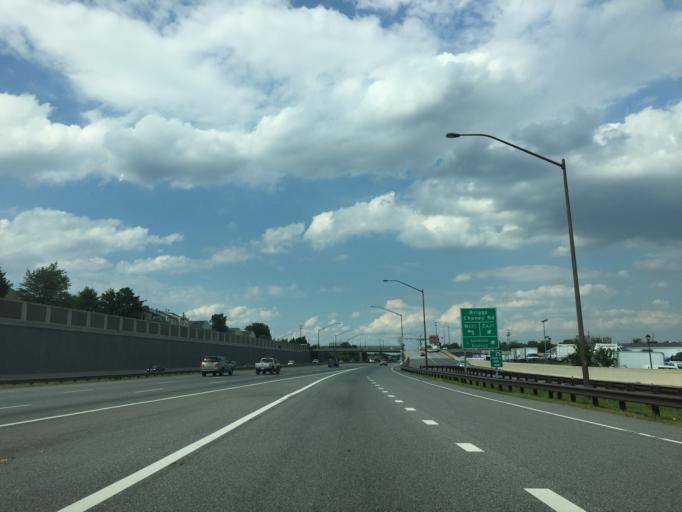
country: US
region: Maryland
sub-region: Montgomery County
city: Fairland
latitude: 39.0801
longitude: -76.9504
